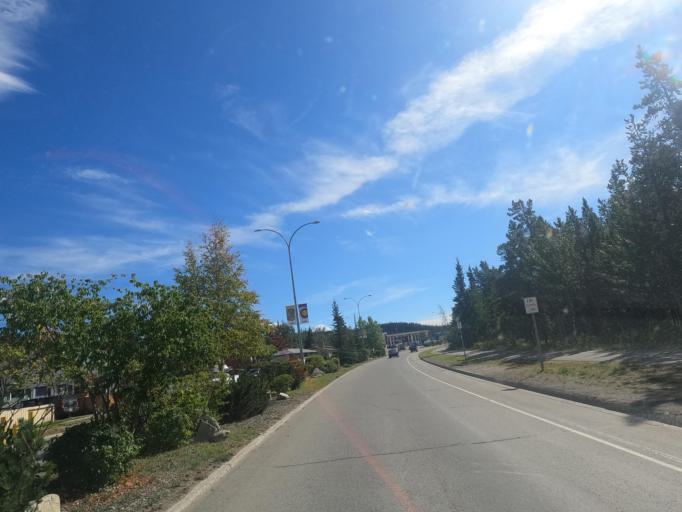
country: CA
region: Yukon
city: Whitehorse
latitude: 60.7083
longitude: -135.0356
